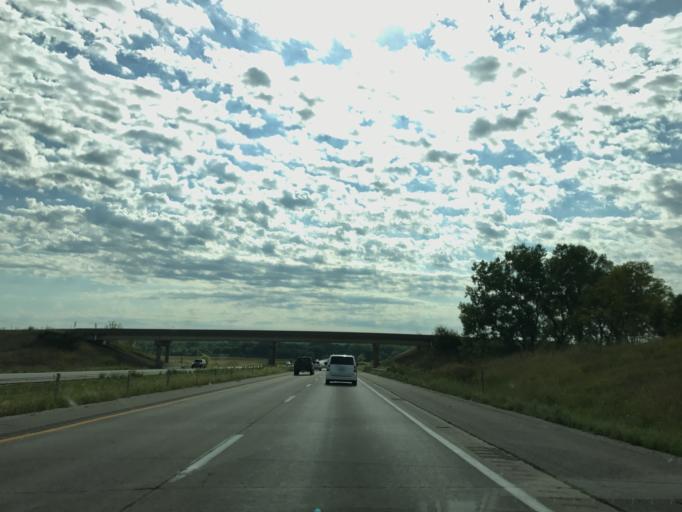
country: US
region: Iowa
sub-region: Dallas County
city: Van Meter
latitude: 41.5485
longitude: -93.9521
